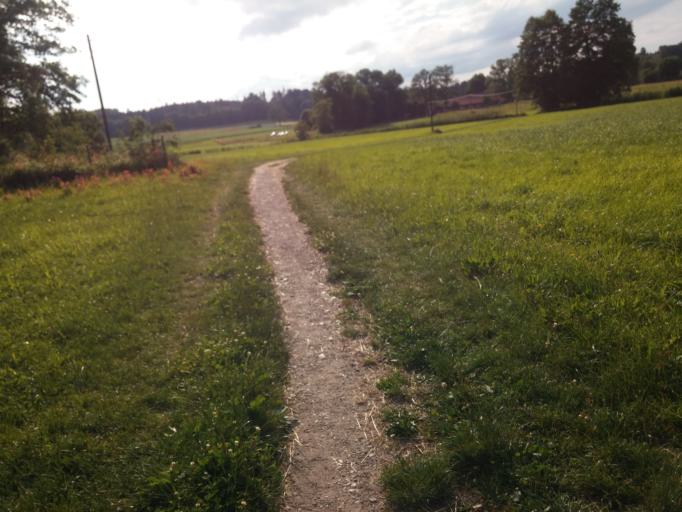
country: DE
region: Bavaria
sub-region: Upper Bavaria
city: Moosach
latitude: 48.0196
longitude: 11.8585
